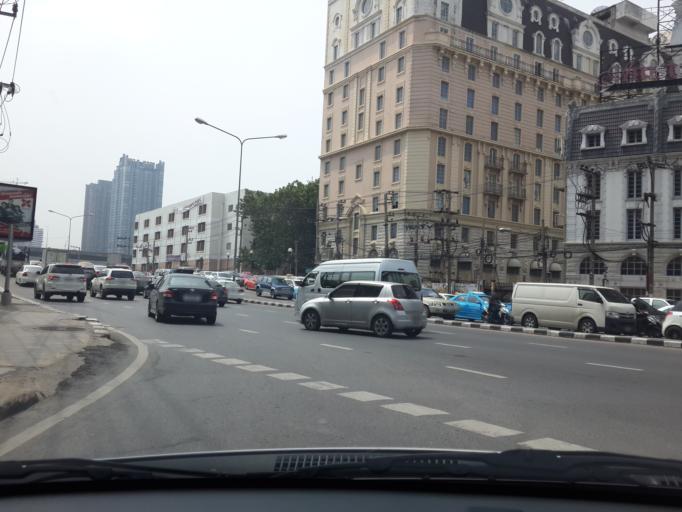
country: TH
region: Bangkok
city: Din Daeng
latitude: 13.7557
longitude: 100.5651
